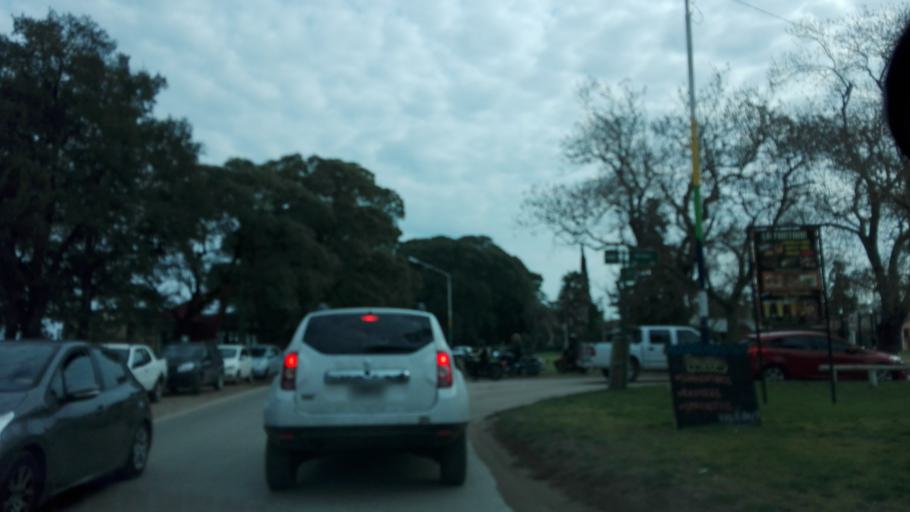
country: AR
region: Buenos Aires
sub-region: Partido de Chascomus
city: Chascomus
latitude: -35.5835
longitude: -58.0066
